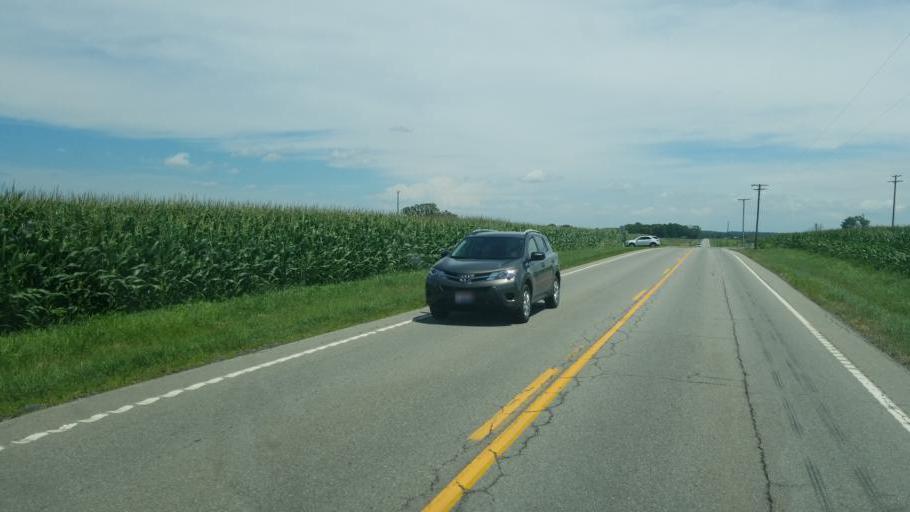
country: US
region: Ohio
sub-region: Richland County
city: Shelby
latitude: 40.8944
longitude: -82.5578
